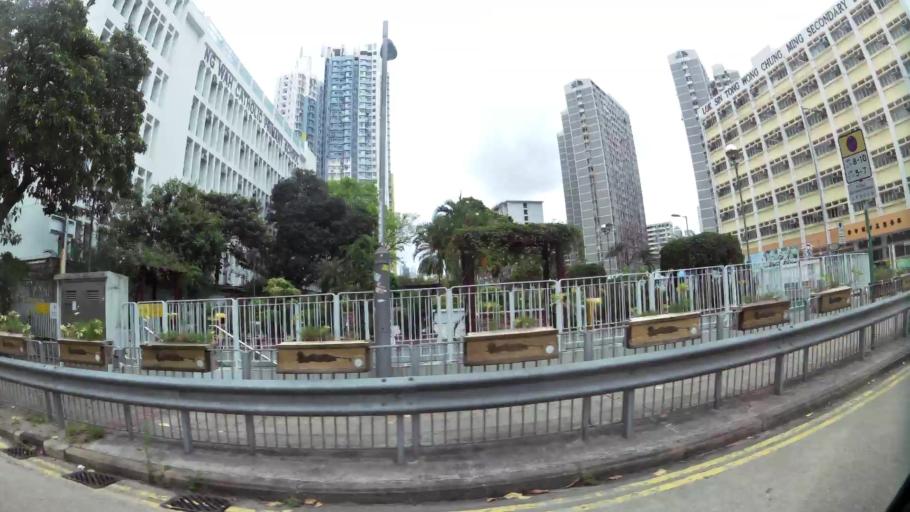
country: HK
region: Wong Tai Sin
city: Wong Tai Sin
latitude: 22.3336
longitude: 114.1950
